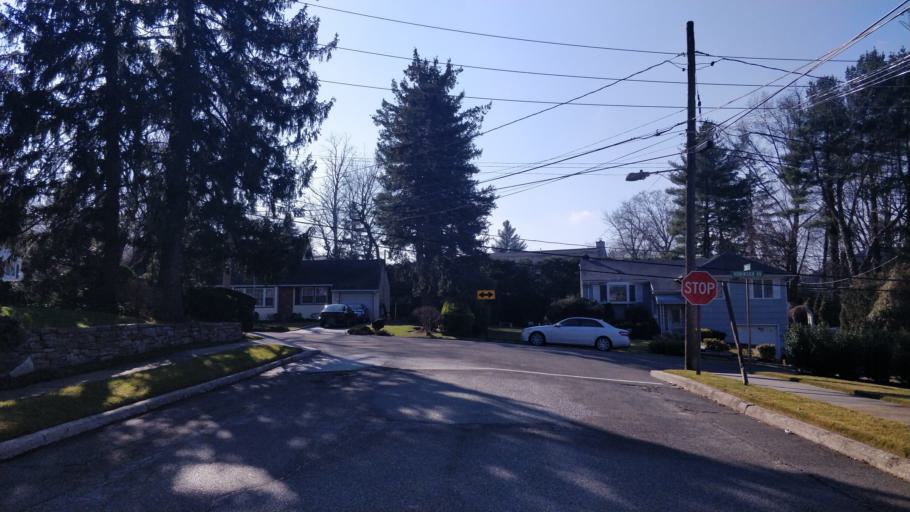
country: US
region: New York
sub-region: Nassau County
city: Glen Cove
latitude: 40.8581
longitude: -73.6324
